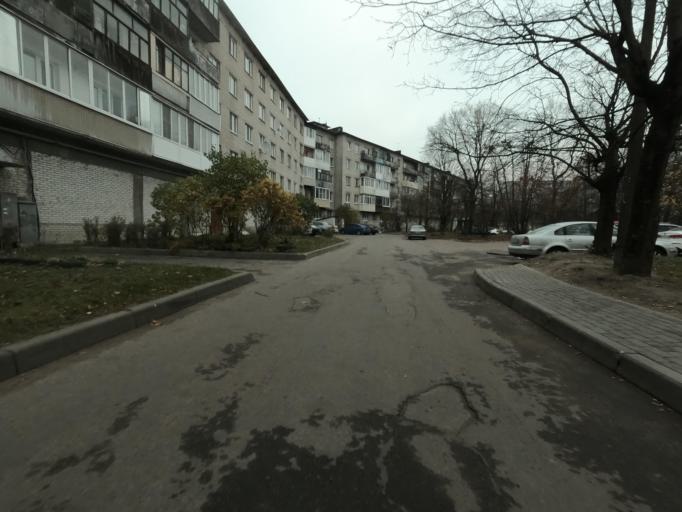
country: RU
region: Leningrad
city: Kirovsk
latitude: 59.8878
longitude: 30.9910
